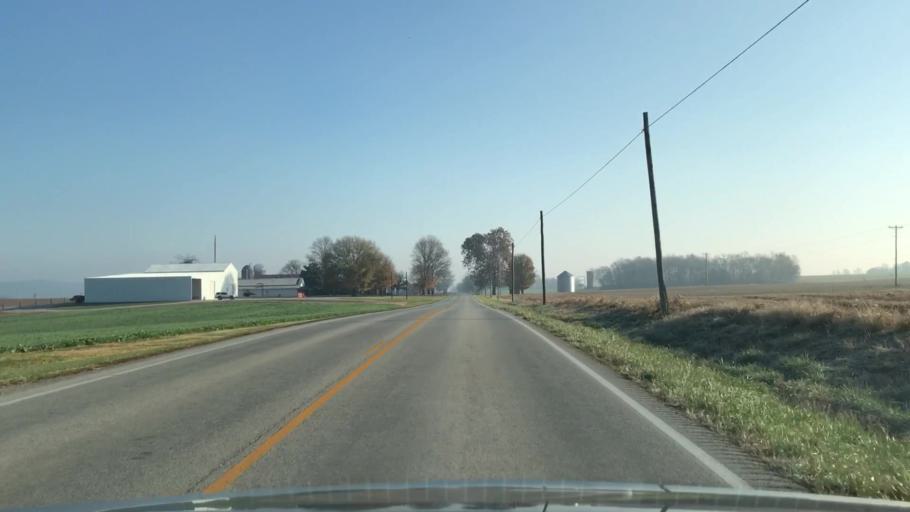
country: US
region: Kentucky
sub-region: Edmonson County
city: Brownsville
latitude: 37.0781
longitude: -86.2470
